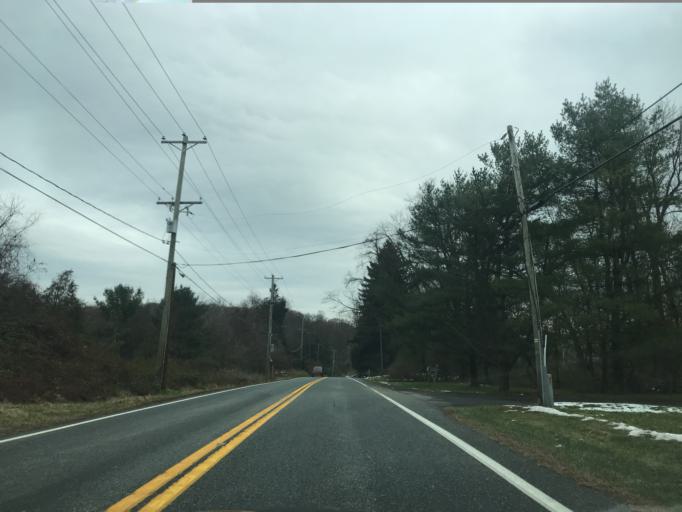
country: US
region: Pennsylvania
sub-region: York County
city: Susquehanna Trails
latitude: 39.6648
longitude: -76.3479
